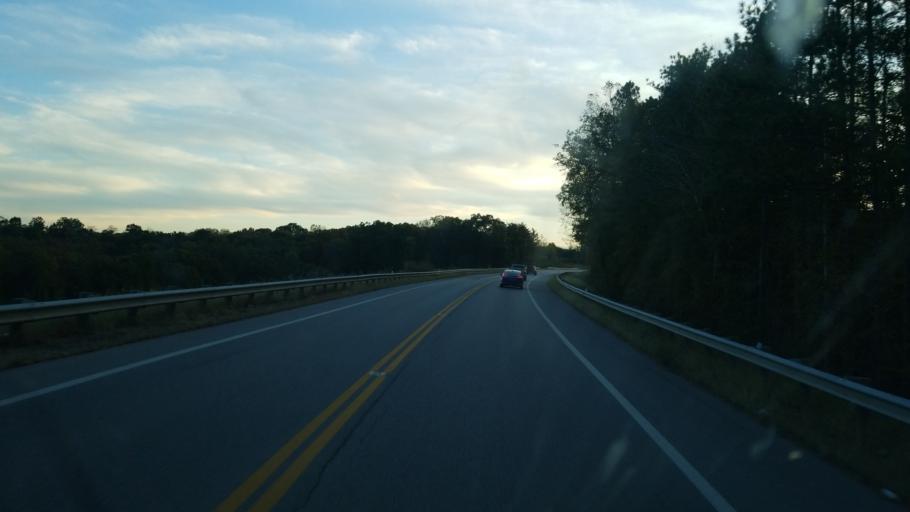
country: US
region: West Virginia
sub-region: Mason County
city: New Haven
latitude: 39.1403
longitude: -81.8558
